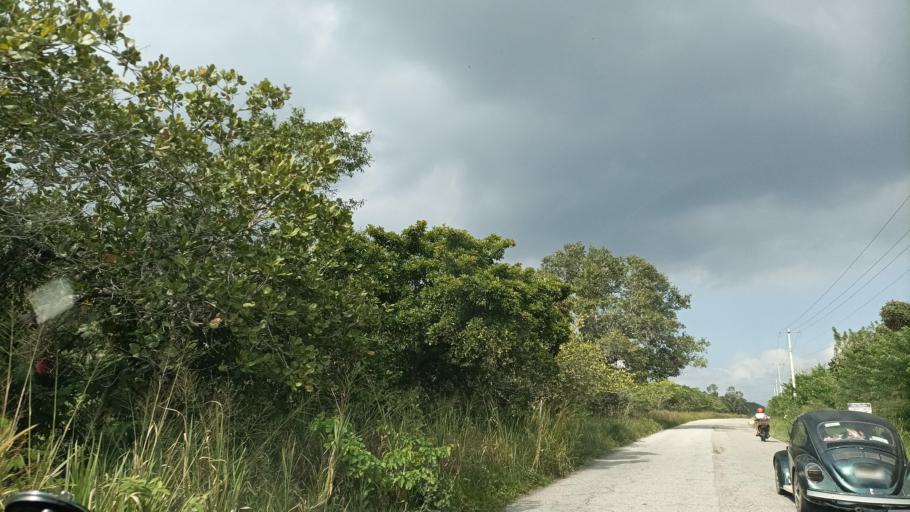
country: MX
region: Veracruz
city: Las Choapas
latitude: 17.8297
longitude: -94.1059
